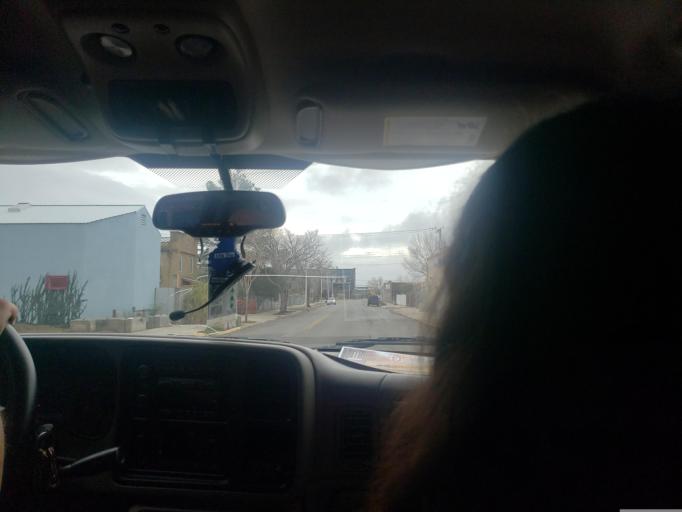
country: US
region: New Mexico
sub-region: Bernalillo County
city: Albuquerque
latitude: 35.0785
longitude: -106.6504
